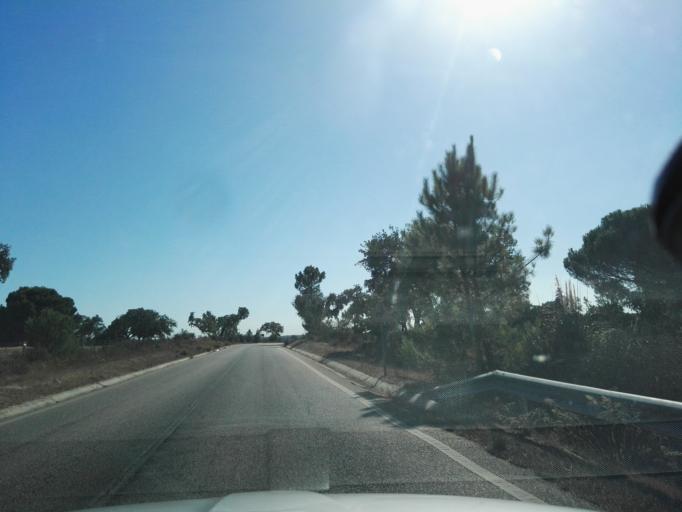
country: PT
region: Santarem
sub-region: Benavente
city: Poceirao
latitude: 38.8789
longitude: -8.7446
